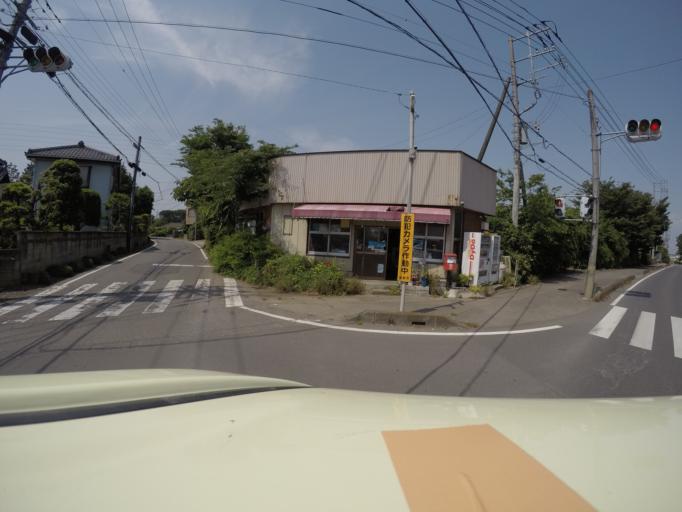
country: JP
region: Ibaraki
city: Iwai
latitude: 36.0497
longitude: 139.9051
